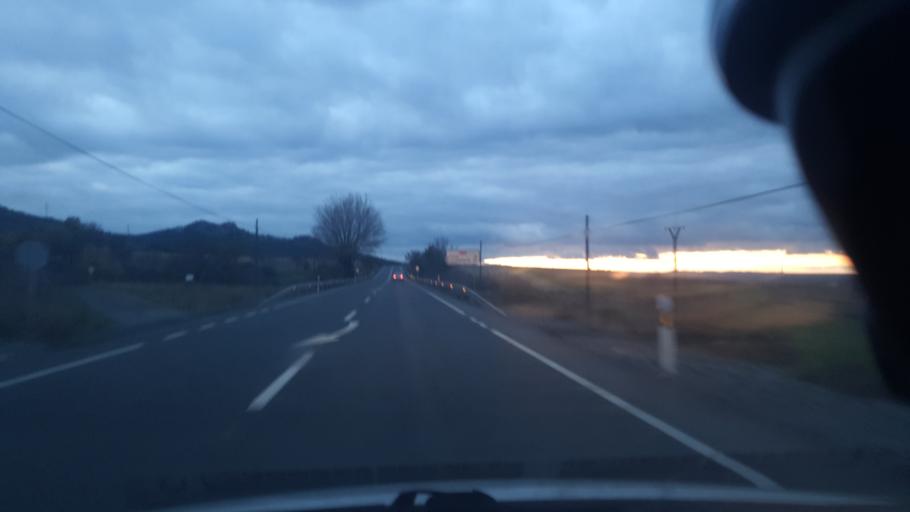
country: ES
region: Castille and Leon
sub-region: Provincia de Avila
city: Ojos-Albos
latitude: 40.7403
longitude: -4.4762
